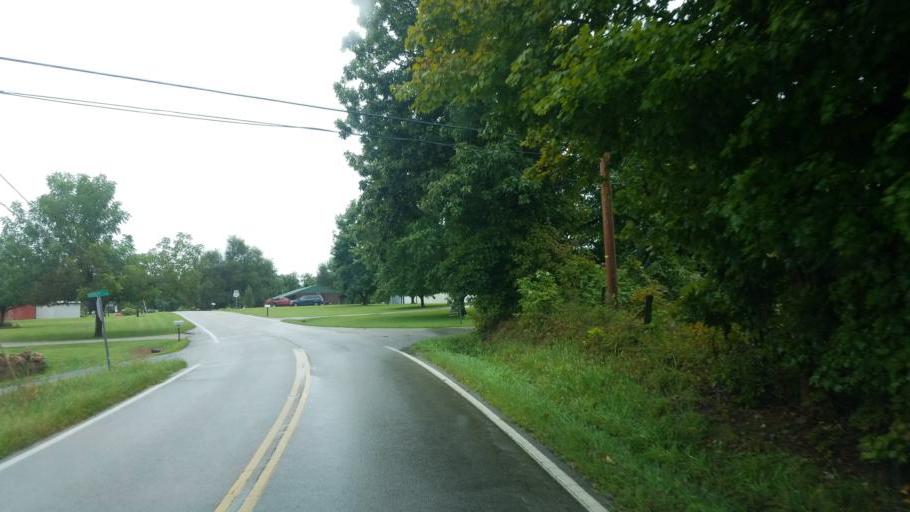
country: US
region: Ohio
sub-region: Adams County
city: West Union
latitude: 38.7282
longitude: -83.5178
